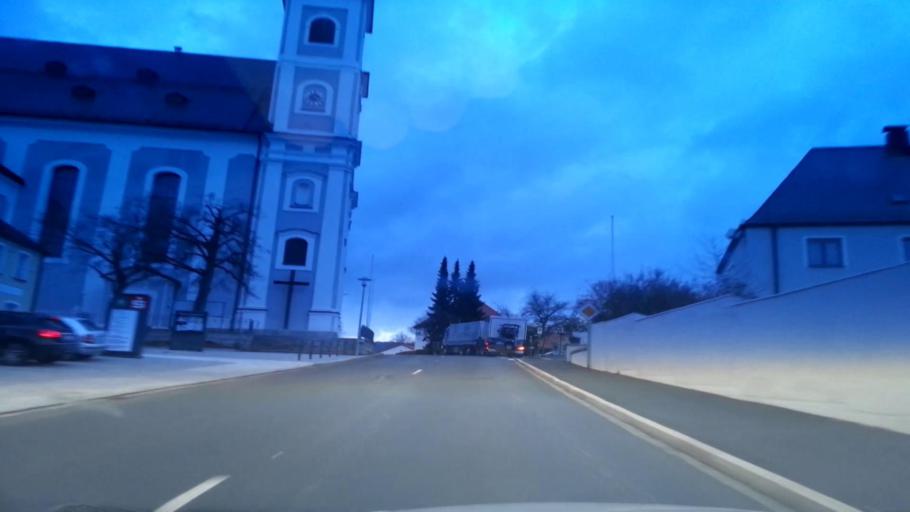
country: DE
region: Bavaria
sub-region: Upper Palatinate
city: Fuchsmuhl
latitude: 49.9261
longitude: 12.1434
